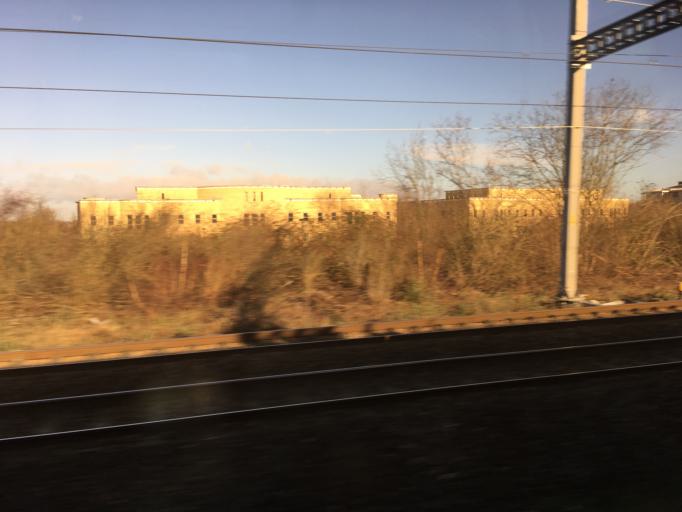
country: GB
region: England
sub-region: Wokingham
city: Earley
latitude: 51.4594
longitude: -0.9304
